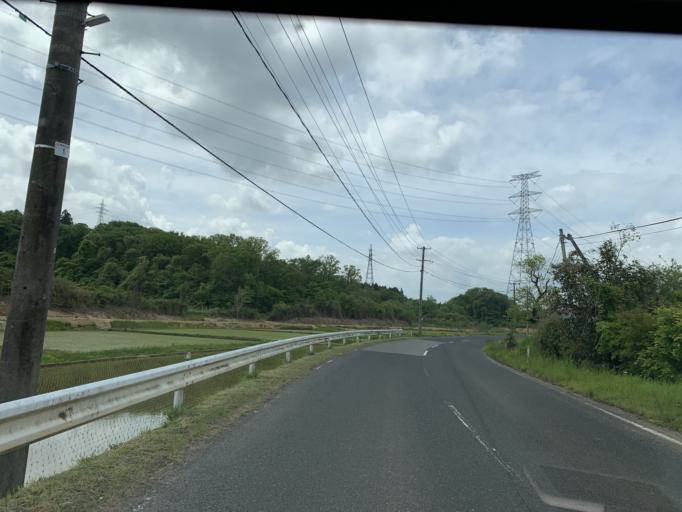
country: JP
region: Iwate
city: Ichinoseki
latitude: 38.8115
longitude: 141.0205
